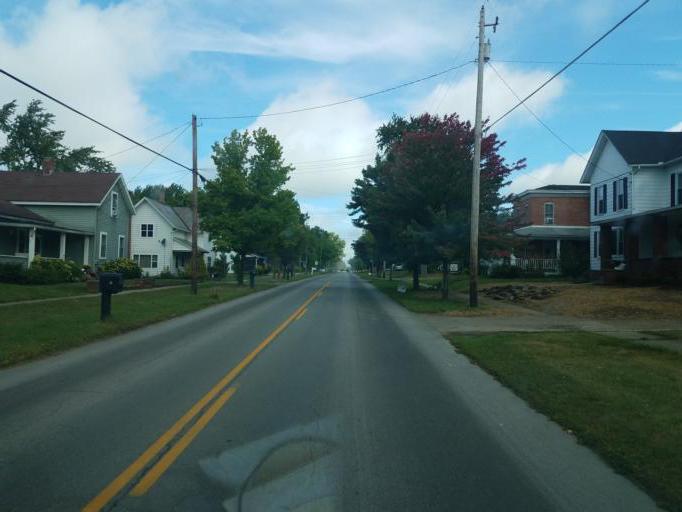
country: US
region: Ohio
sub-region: Wayne County
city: West Salem
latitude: 40.9745
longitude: -82.1097
